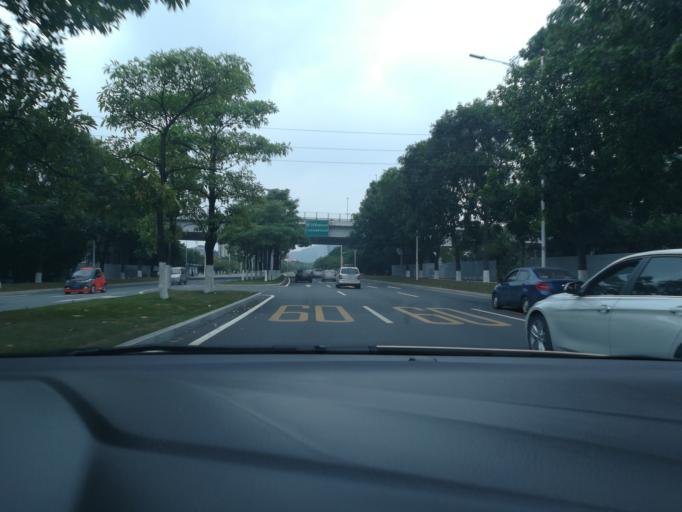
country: CN
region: Guangdong
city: Nansha
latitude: 22.7823
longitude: 113.5927
